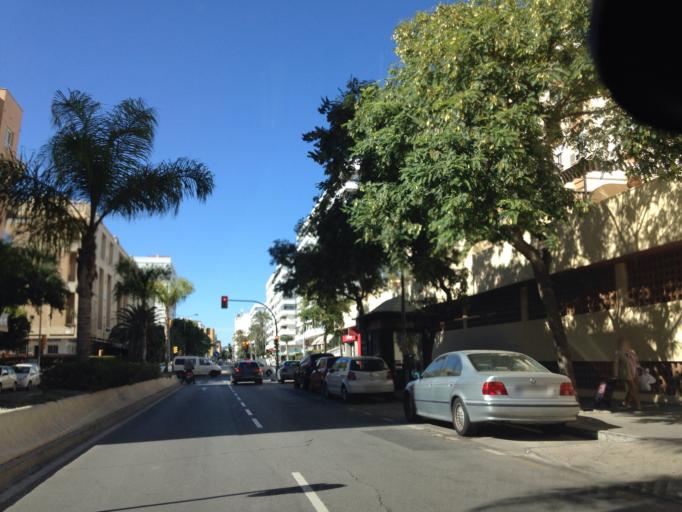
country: ES
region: Andalusia
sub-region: Provincia de Malaga
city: Malaga
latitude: 36.6949
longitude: -4.4422
